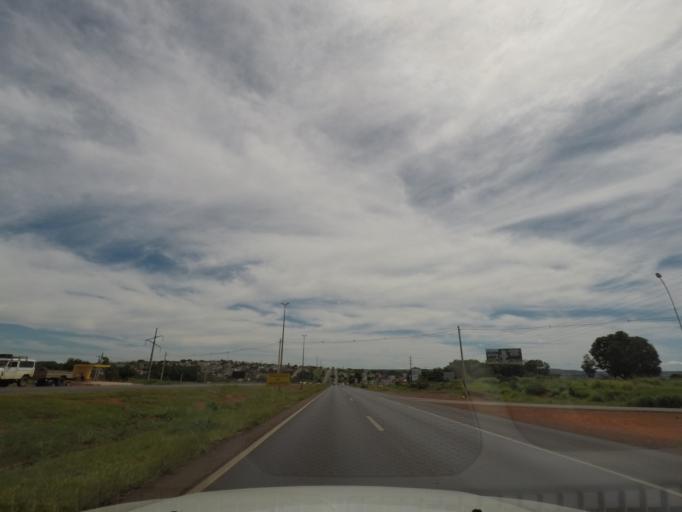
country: BR
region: Goias
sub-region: Planaltina
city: Planaltina
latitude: -15.6113
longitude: -47.6981
